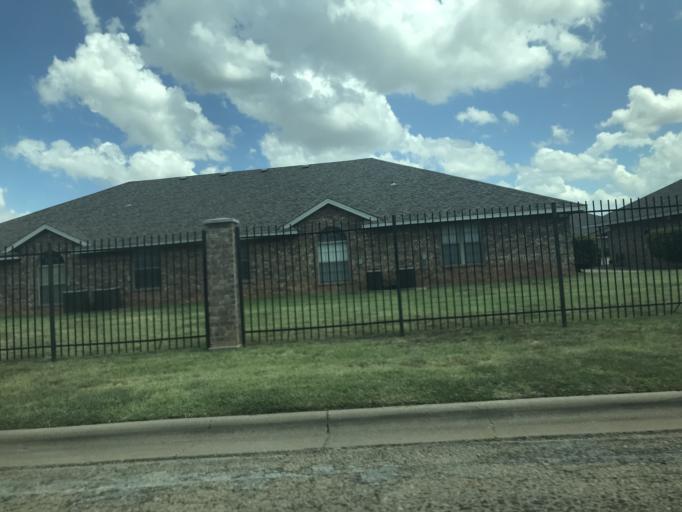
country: US
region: Texas
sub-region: Taylor County
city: Abilene
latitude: 32.4437
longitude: -99.6983
